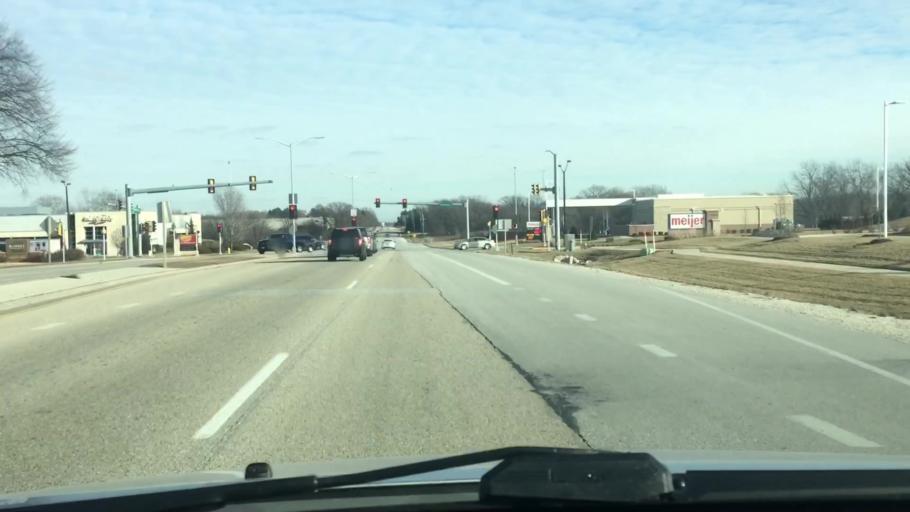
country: US
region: Wisconsin
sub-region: Waukesha County
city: Sussex
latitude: 43.1121
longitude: -88.2428
